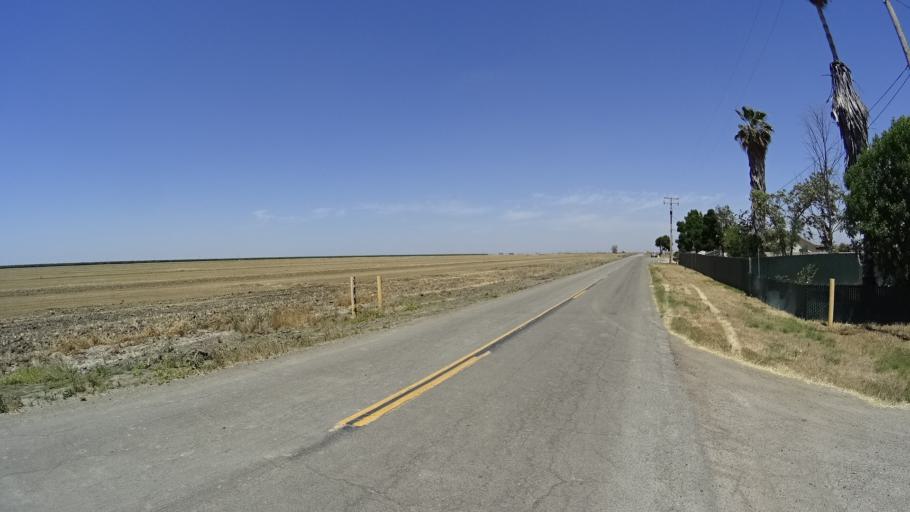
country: US
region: California
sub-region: Kings County
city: Corcoran
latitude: 36.1180
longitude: -119.5811
